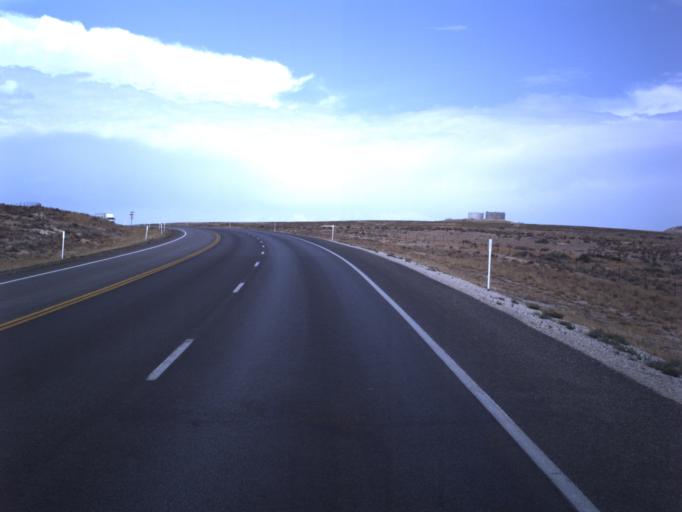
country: US
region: Utah
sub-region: Sanpete County
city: Gunnison
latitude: 39.1656
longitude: -111.8189
